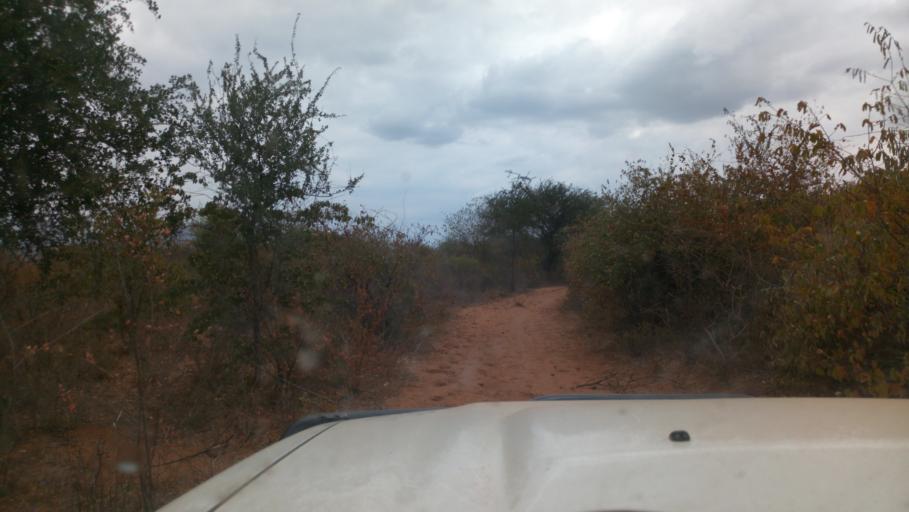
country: KE
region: Kitui
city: Kitui
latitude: -1.8496
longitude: 38.3982
